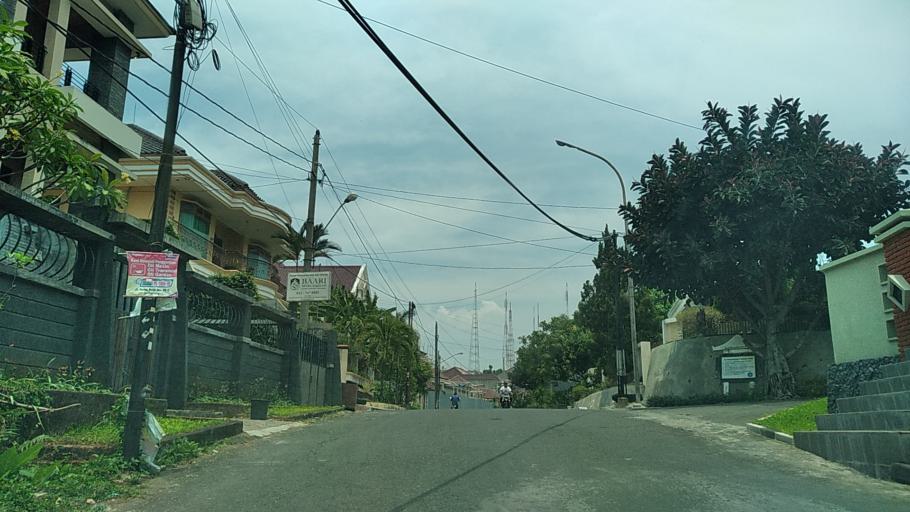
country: ID
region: Central Java
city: Semarang
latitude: -7.0438
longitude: 110.4158
